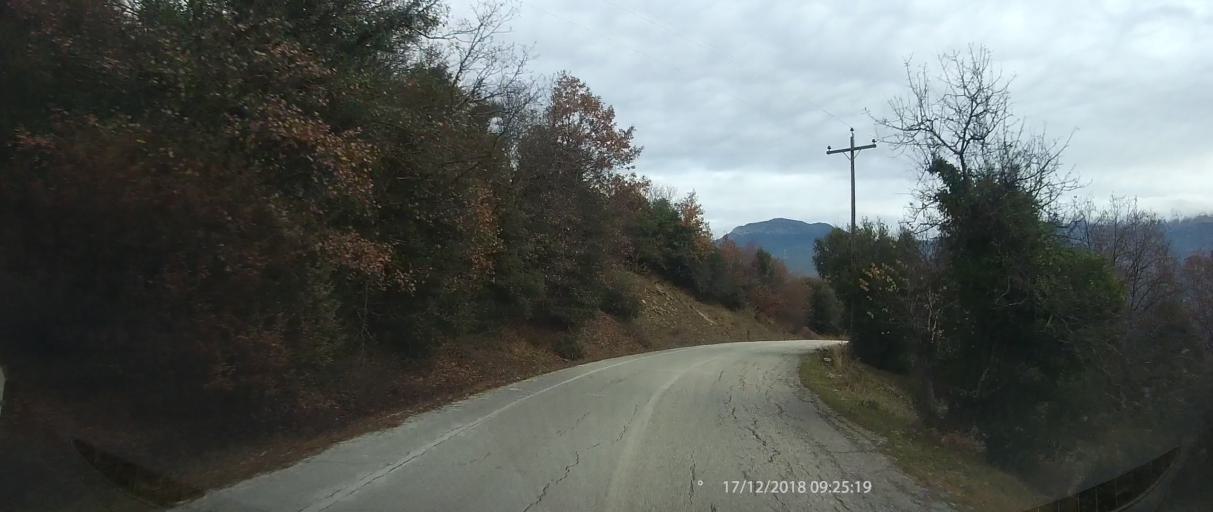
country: GR
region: Epirus
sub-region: Nomos Ioanninon
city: Kalpaki
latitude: 39.9379
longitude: 20.6715
